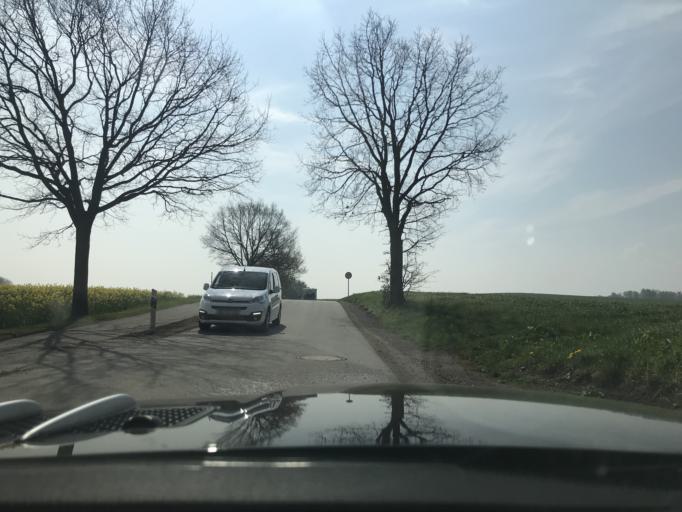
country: DE
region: Schleswig-Holstein
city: Schashagen
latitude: 54.1267
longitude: 10.9183
